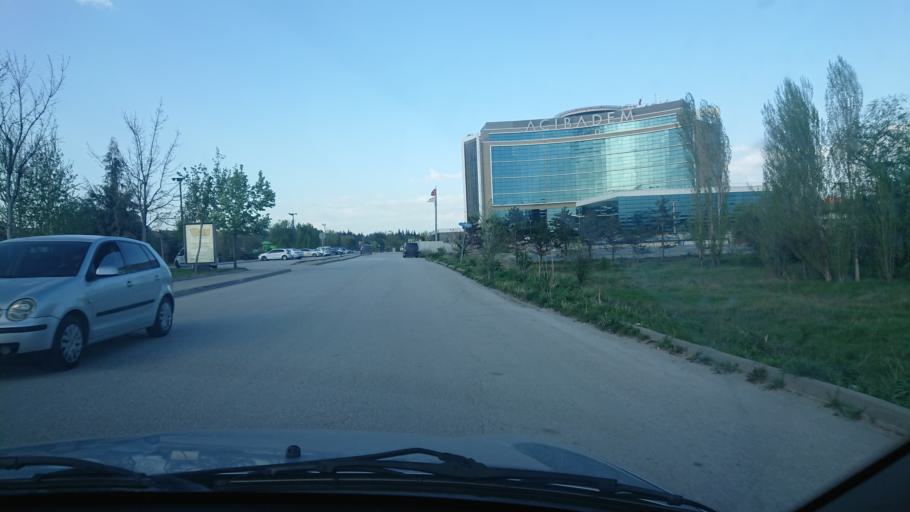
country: TR
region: Eskisehir
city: Eskisehir
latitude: 39.7845
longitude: 30.4933
